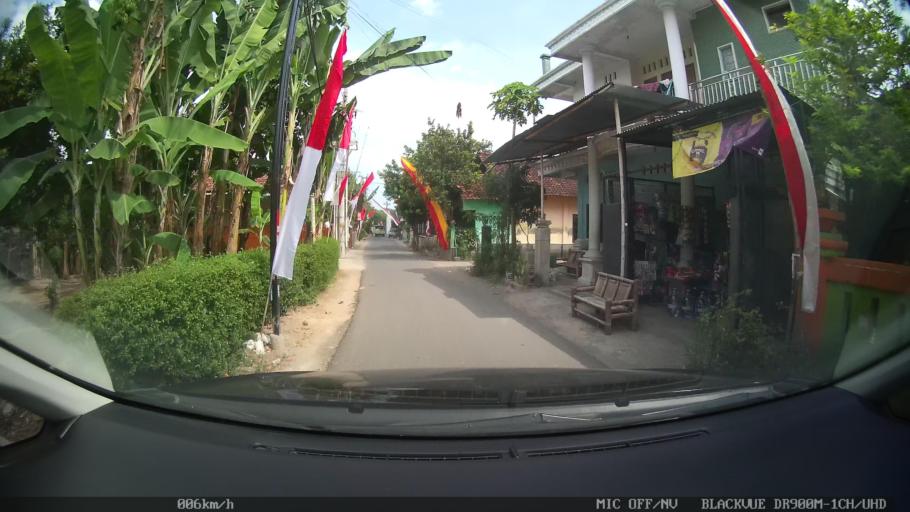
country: ID
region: Daerah Istimewa Yogyakarta
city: Kasihan
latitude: -7.8205
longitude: 110.3324
